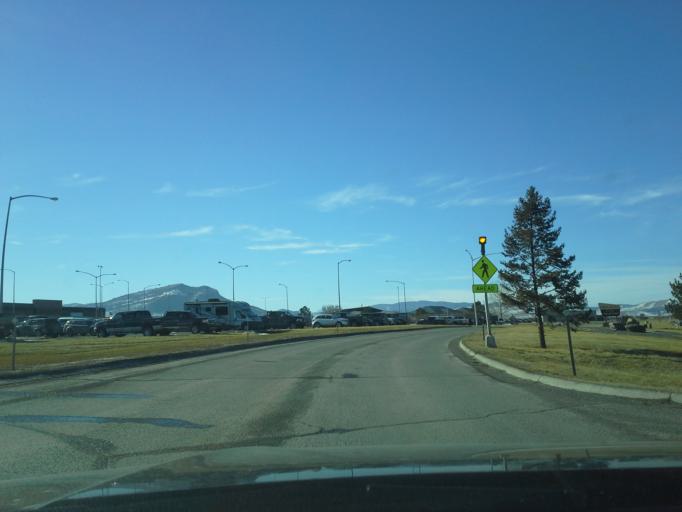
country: US
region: Montana
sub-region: Lewis and Clark County
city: Helena
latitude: 46.6116
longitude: -111.9883
